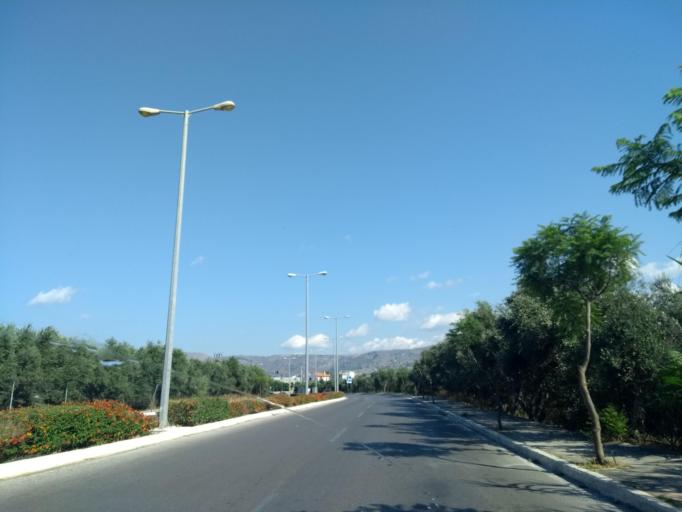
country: GR
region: Crete
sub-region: Nomos Chanias
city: Perivolia
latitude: 35.5055
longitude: 24.0049
